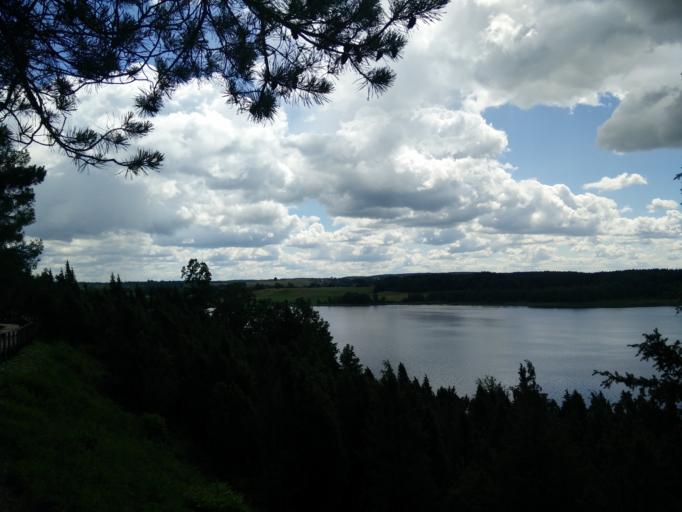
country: LT
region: Kauno apskritis
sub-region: Kauno rajonas
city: Karmelava
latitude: 54.8128
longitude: 24.1819
